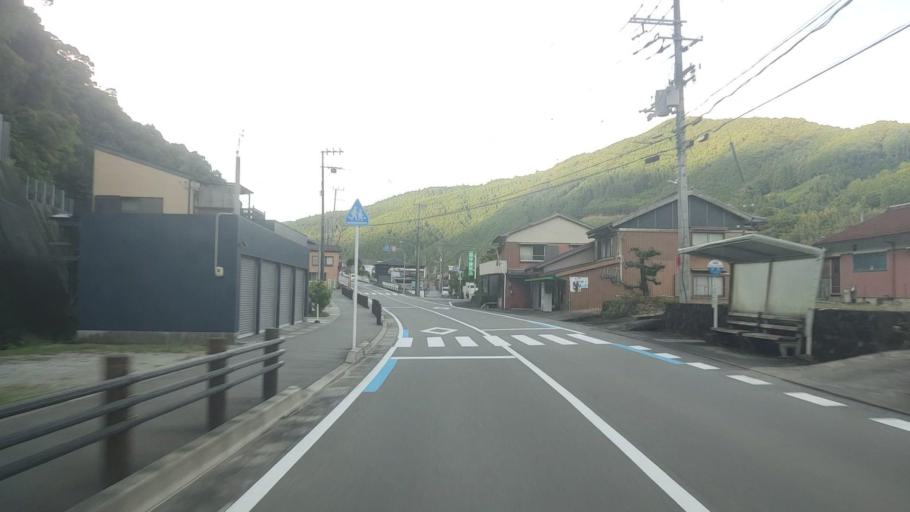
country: JP
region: Wakayama
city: Tanabe
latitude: 33.7887
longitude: 135.5142
